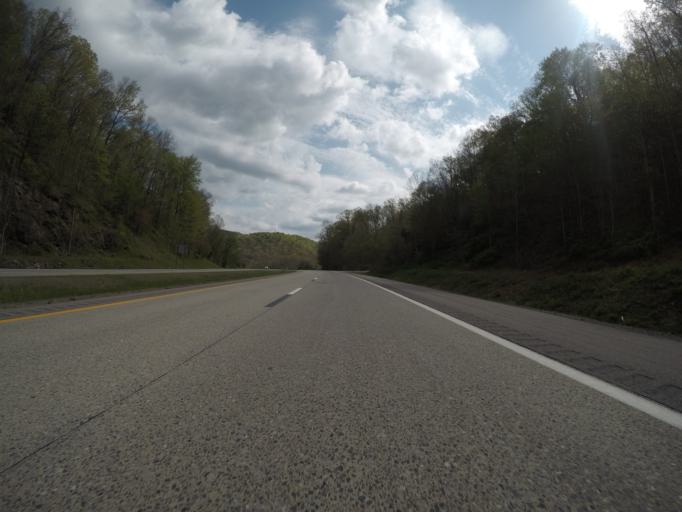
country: US
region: West Virginia
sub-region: Kanawha County
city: Alum Creek
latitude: 38.2022
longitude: -81.8343
